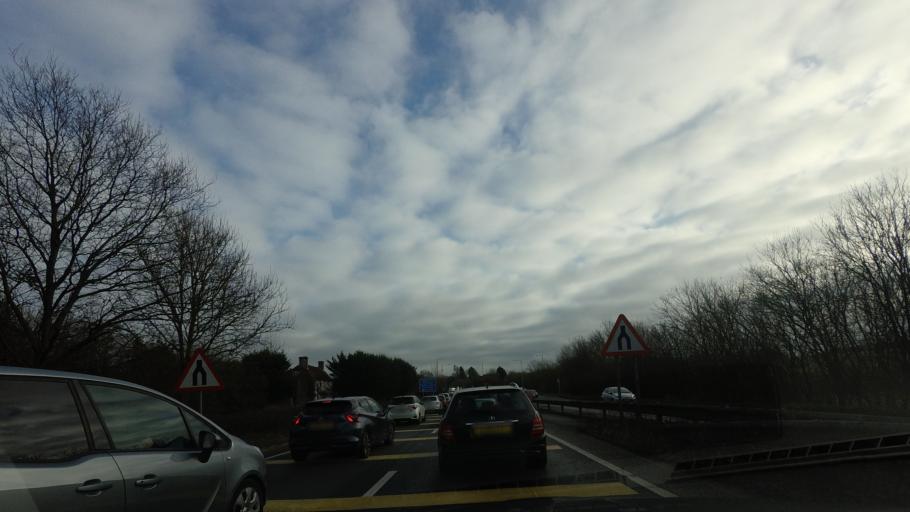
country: GB
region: England
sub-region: Kent
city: Pembury
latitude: 51.1362
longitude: 0.3474
